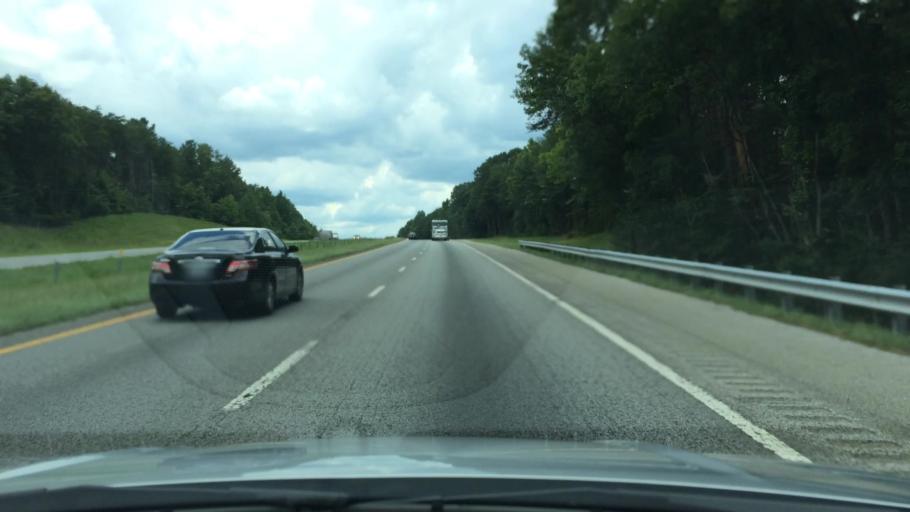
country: US
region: South Carolina
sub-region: Spartanburg County
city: Roebuck
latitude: 34.7940
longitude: -81.9566
